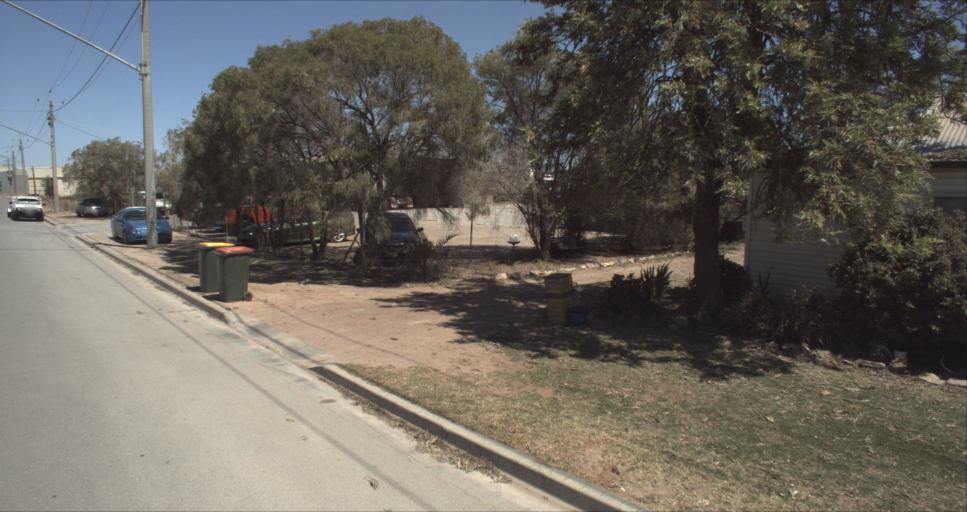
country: AU
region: New South Wales
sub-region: Leeton
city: Leeton
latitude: -34.5482
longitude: 146.3988
